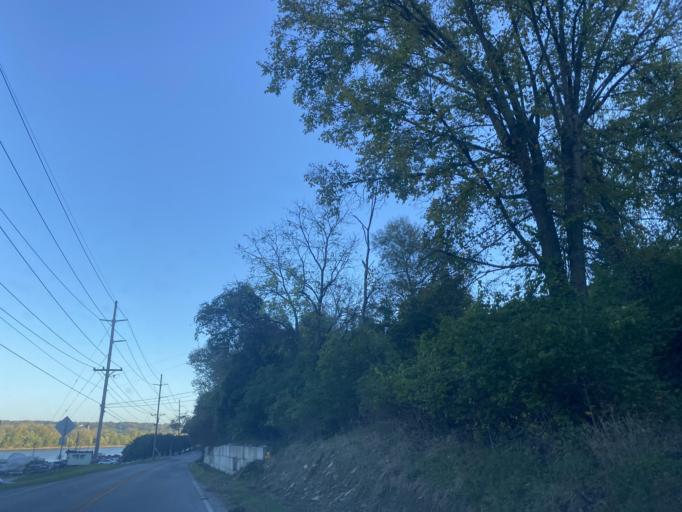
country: US
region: Kentucky
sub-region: Campbell County
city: Dayton
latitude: 39.1100
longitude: -84.4489
